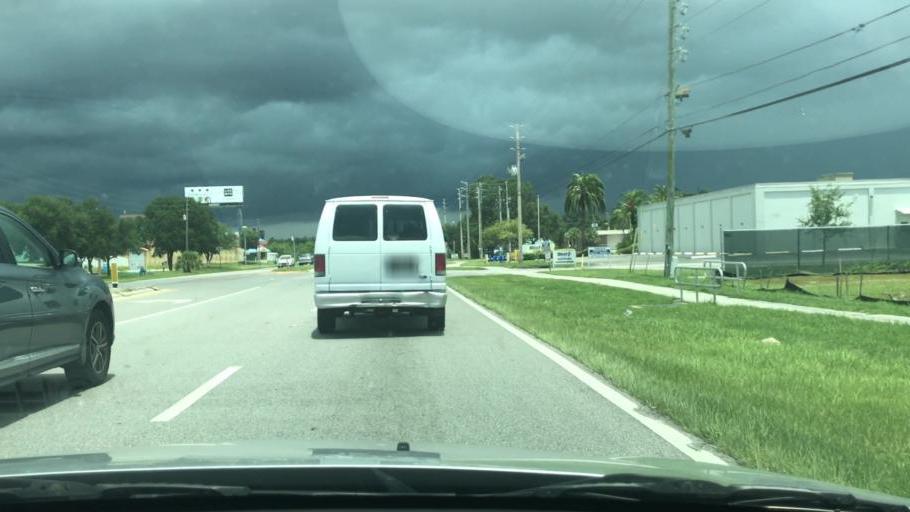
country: US
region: Florida
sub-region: Pinellas County
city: Bay Pines
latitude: 27.8170
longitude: -82.7538
